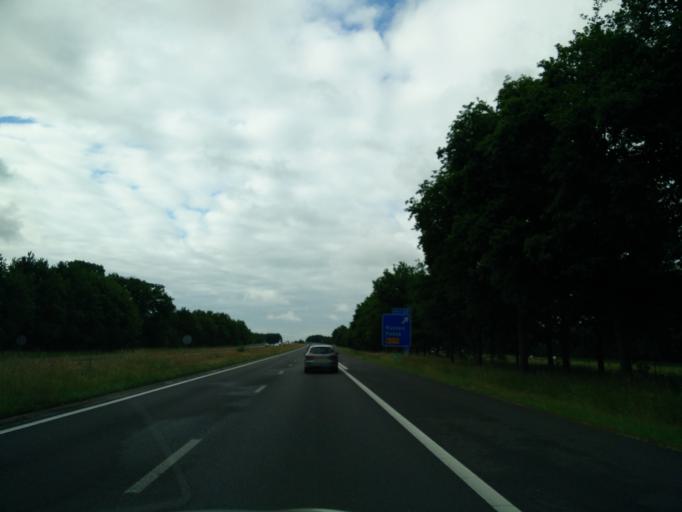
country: NL
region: Drenthe
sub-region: Gemeente Hoogeveen
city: Hoogeveen
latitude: 52.7812
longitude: 6.4469
